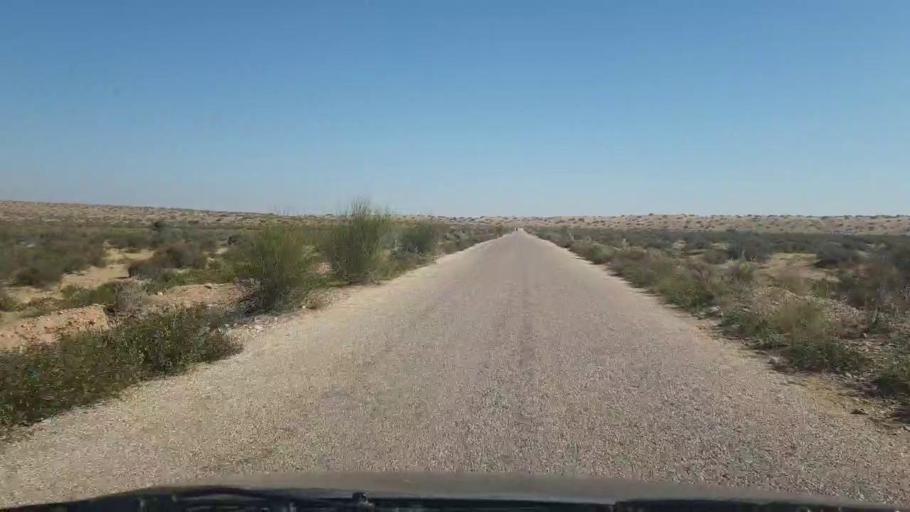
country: PK
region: Sindh
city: Bozdar
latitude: 27.0004
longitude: 68.8257
